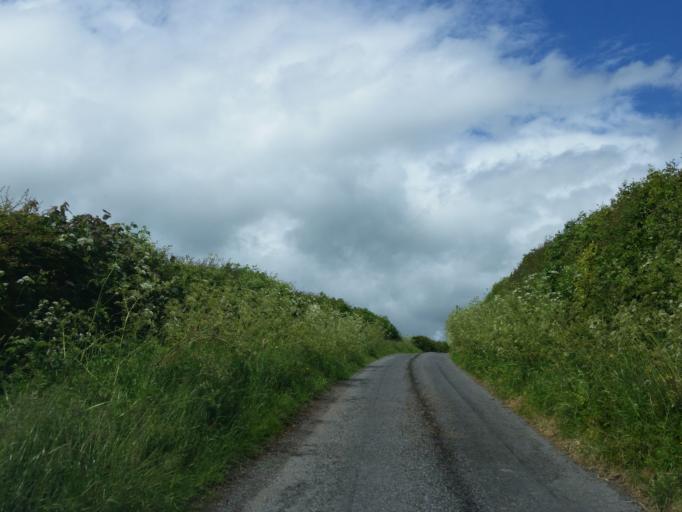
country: GB
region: Northern Ireland
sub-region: Omagh District
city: Omagh
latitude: 54.5446
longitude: -7.1359
